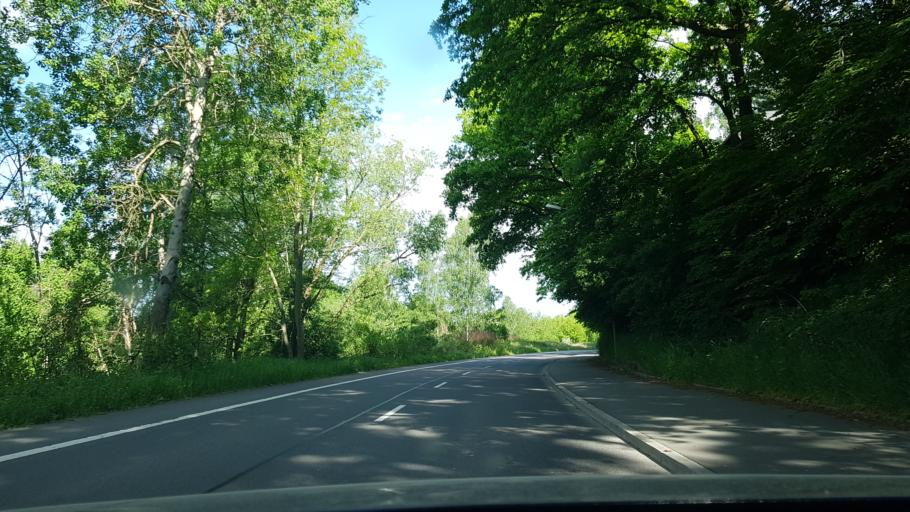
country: DE
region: Saxony
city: Wittgensdorf
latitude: 50.8788
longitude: 12.9026
